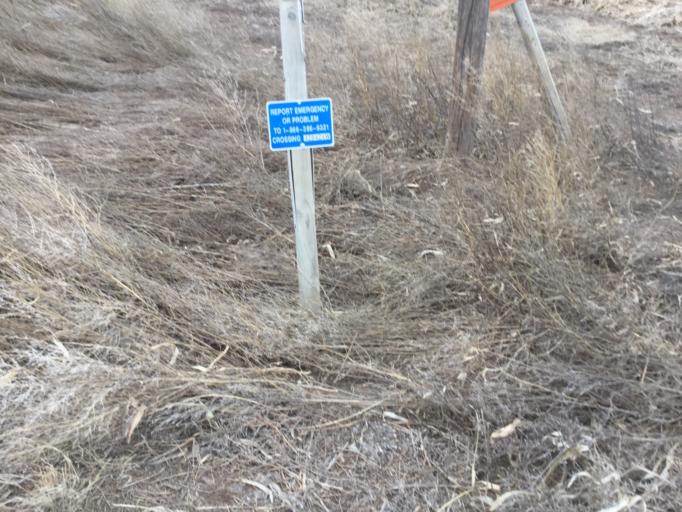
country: US
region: Kansas
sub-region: Scott County
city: Scott City
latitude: 38.5638
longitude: -100.7053
